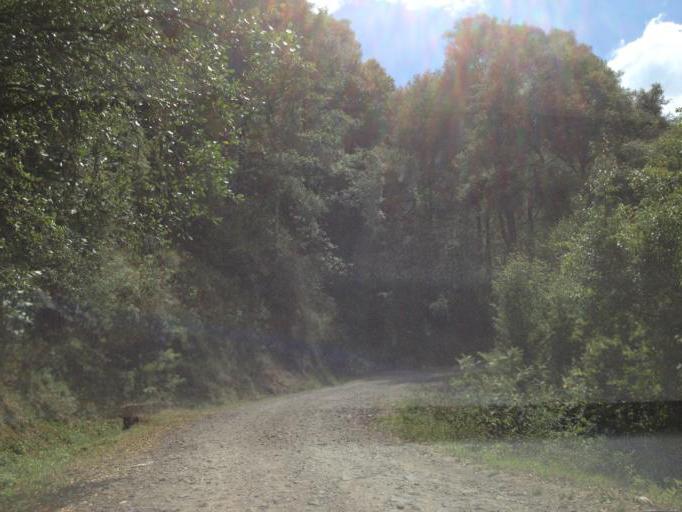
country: MX
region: Hidalgo
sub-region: Pachuca de Soto
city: San Miguel Cerezo (El Cerezo)
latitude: 20.2100
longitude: -98.6823
